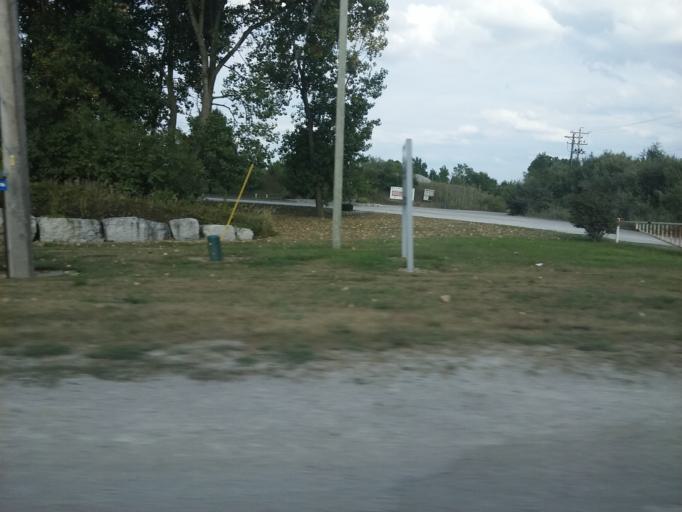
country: US
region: Ohio
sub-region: Wood County
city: Bowling Green
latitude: 41.3122
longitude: -83.6503
